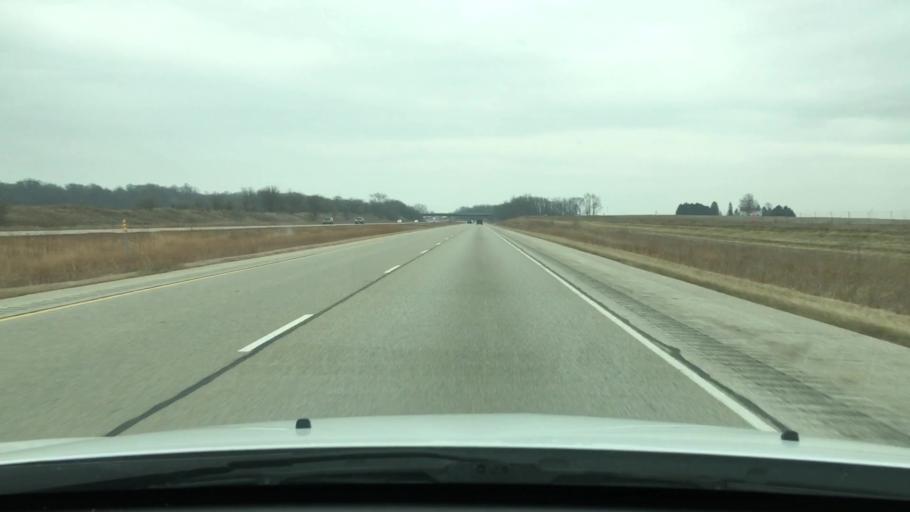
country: US
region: Illinois
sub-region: Logan County
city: Atlanta
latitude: 40.3497
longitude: -89.1222
